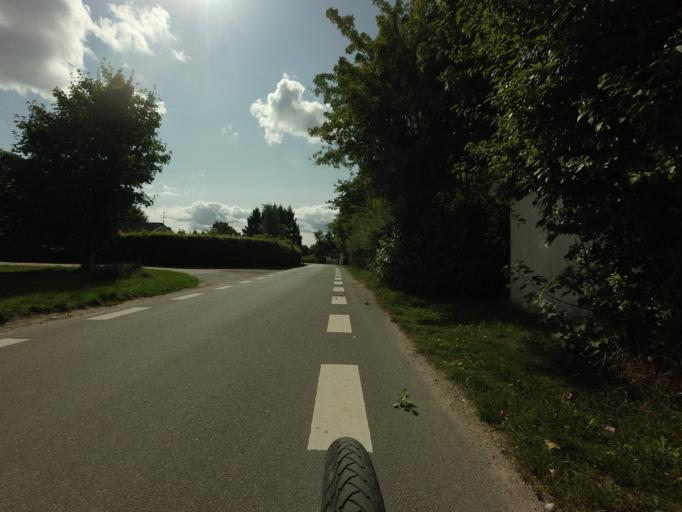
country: DK
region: Zealand
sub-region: Vordingborg Kommune
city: Stege
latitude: 54.9697
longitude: 12.3869
